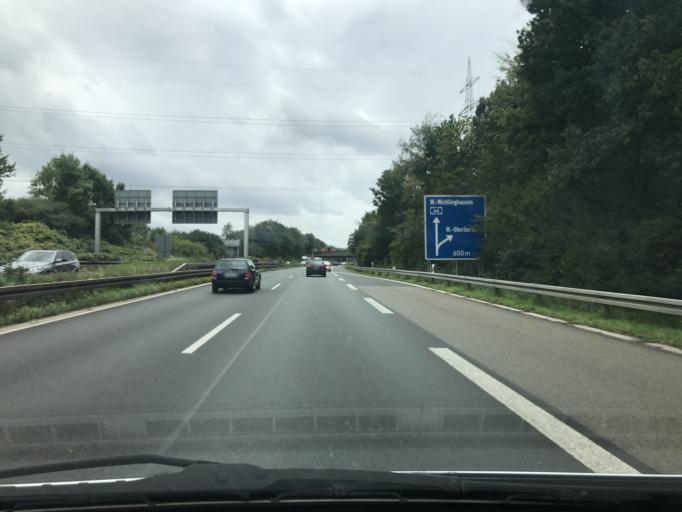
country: DE
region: North Rhine-Westphalia
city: Sprockhovel
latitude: 51.3131
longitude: 7.2599
